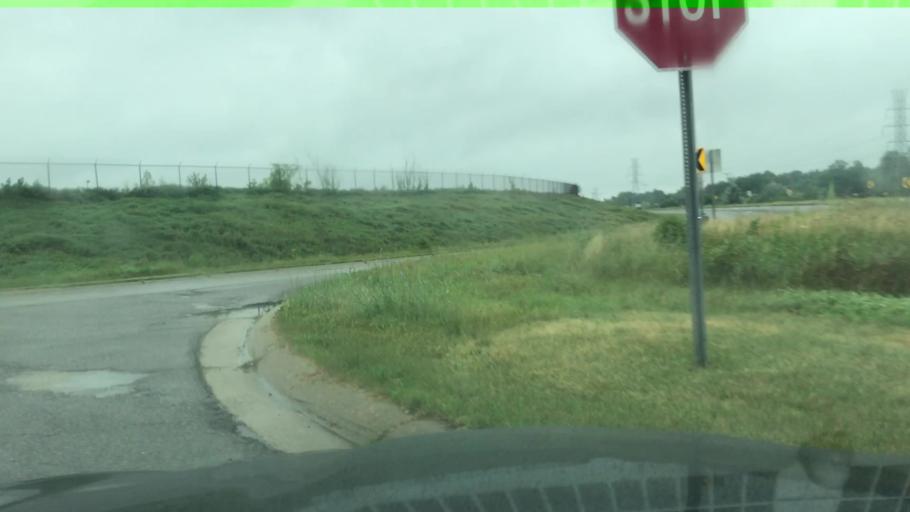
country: US
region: Michigan
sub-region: Oakland County
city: Auburn Hills
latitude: 42.7220
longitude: -83.2662
